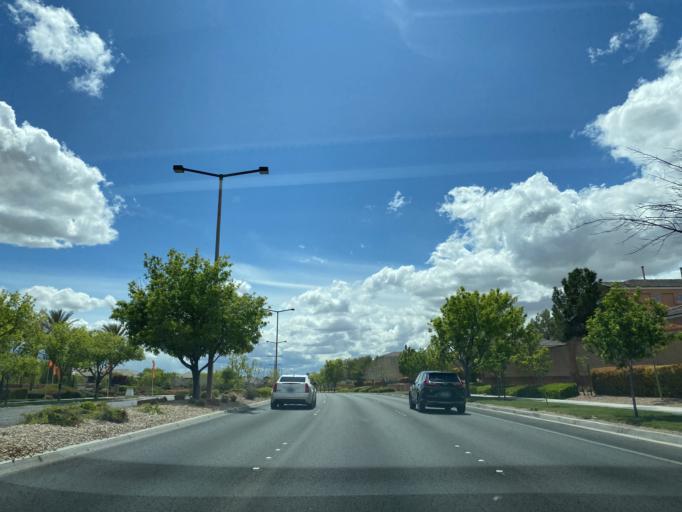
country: US
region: Nevada
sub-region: Clark County
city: Summerlin South
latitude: 36.1665
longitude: -115.3246
